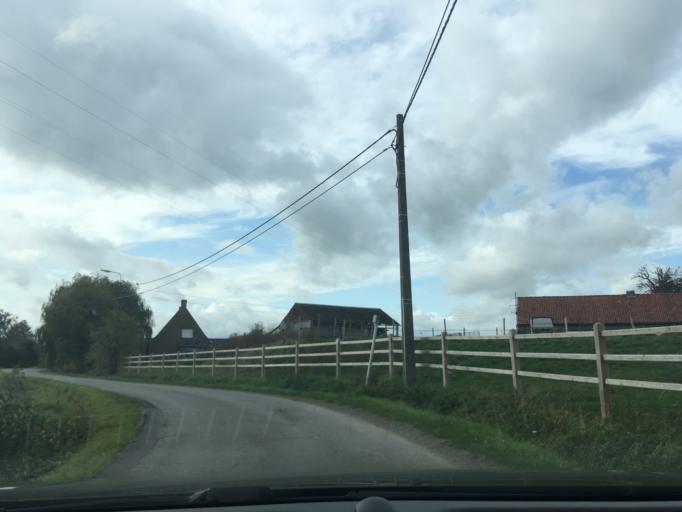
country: BE
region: Flanders
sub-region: Provincie West-Vlaanderen
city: Moorslede
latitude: 50.9112
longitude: 3.0922
